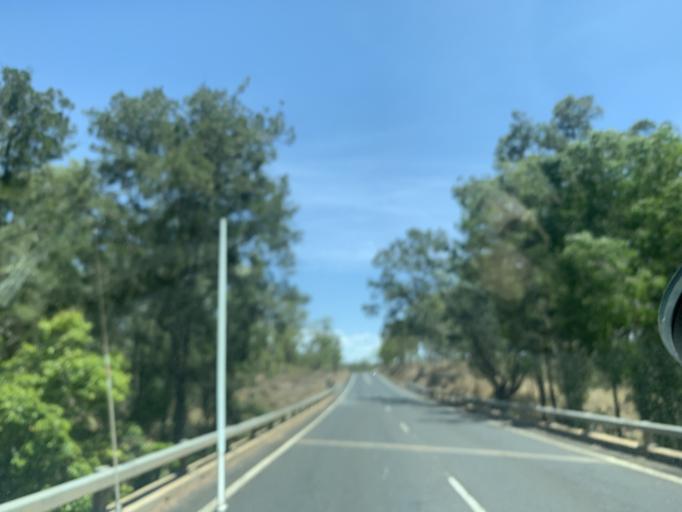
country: AU
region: Queensland
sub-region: Tablelands
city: Mareeba
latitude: -16.9425
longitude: 145.5410
